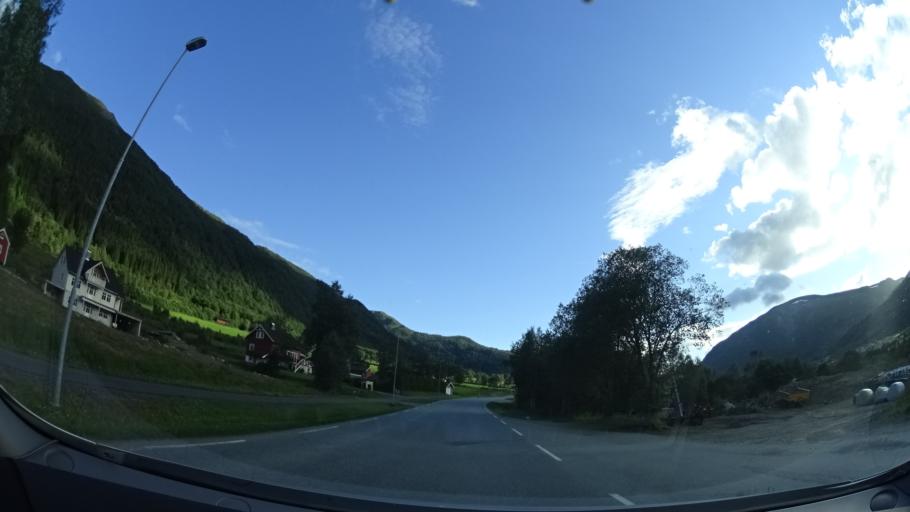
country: NO
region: More og Romsdal
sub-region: Gjemnes
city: Batnfjordsora
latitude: 62.8857
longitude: 7.6710
